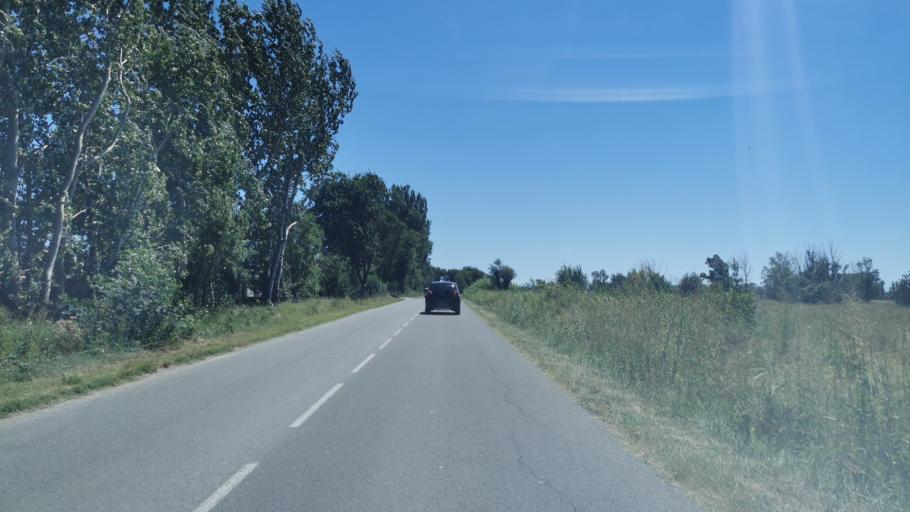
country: FR
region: Languedoc-Roussillon
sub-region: Departement de l'Aude
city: Vinassan
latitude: 43.2216
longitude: 3.0763
